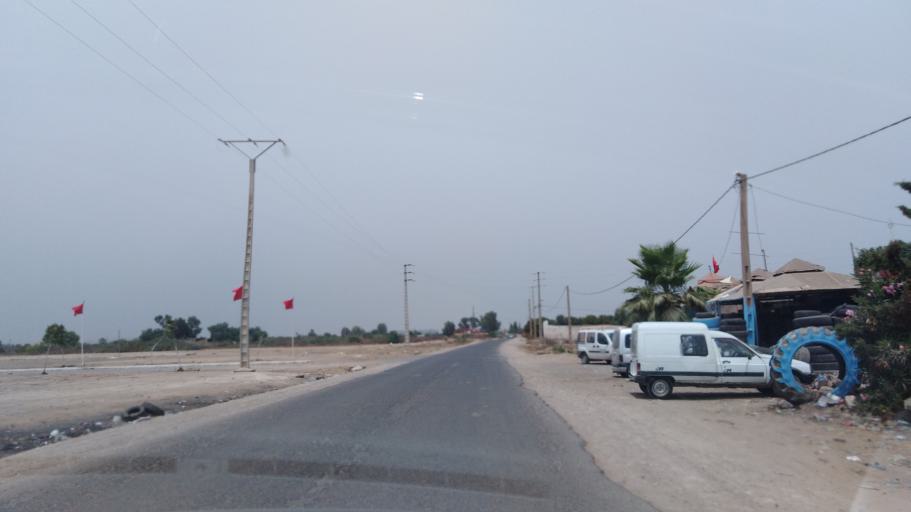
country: MA
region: Grand Casablanca
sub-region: Mediouna
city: Mediouna
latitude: 33.4030
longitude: -7.5128
